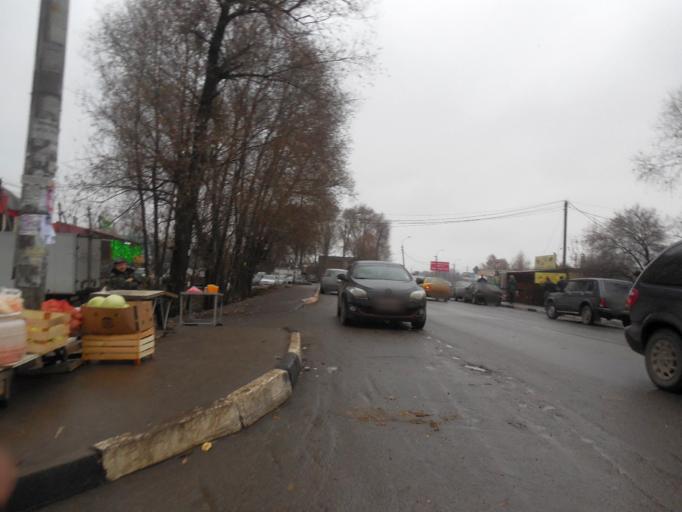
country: RU
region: Moskovskaya
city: Barybino
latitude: 55.2689
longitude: 37.8945
